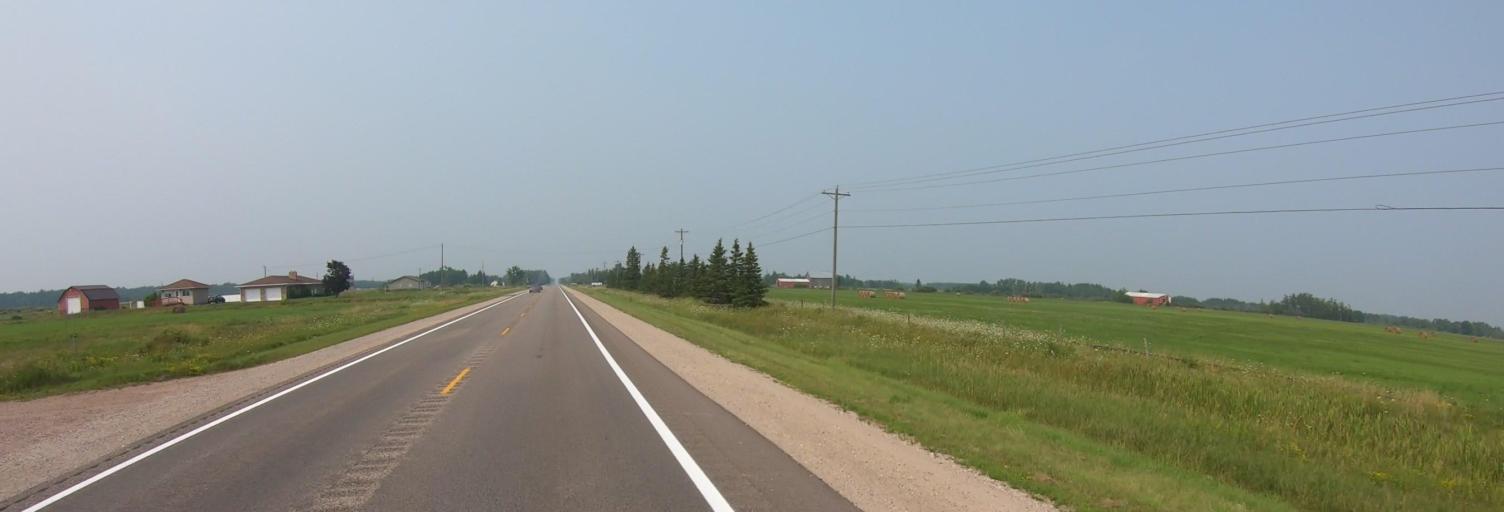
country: US
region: Michigan
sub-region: Chippewa County
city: Sault Ste. Marie
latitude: 46.1693
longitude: -84.3635
